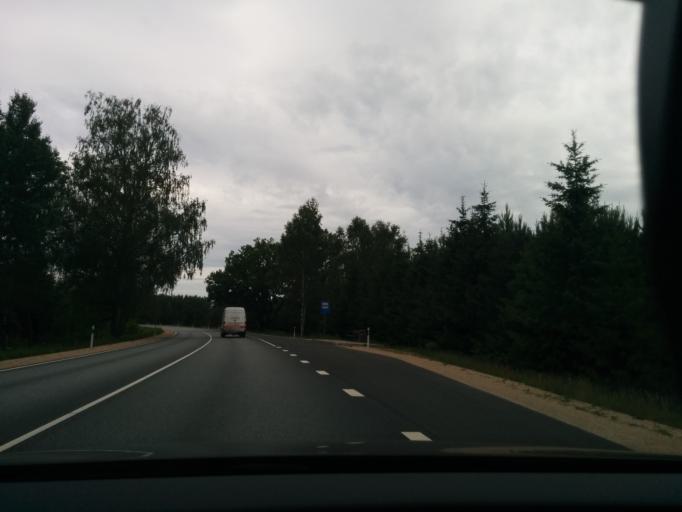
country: LV
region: Ikskile
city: Ikskile
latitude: 56.8920
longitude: 24.4712
